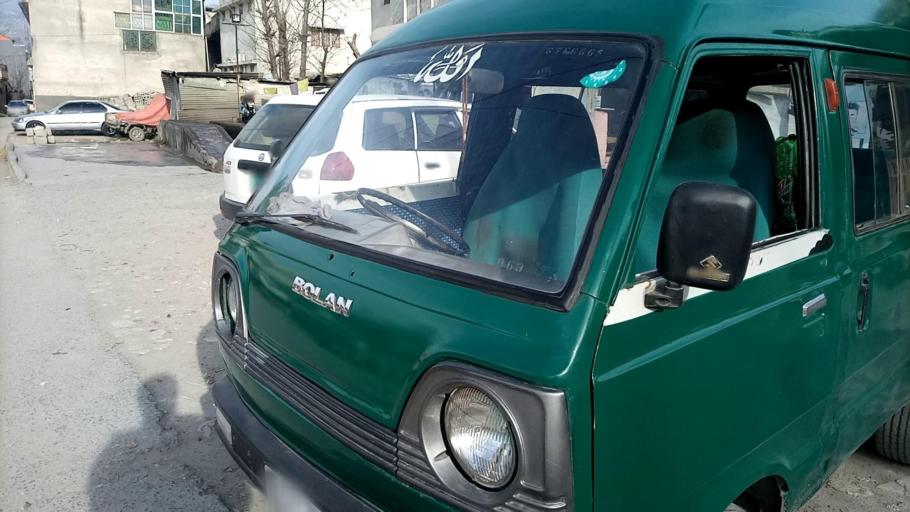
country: PK
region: Khyber Pakhtunkhwa
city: Abbottabad
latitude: 34.1725
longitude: 73.2381
